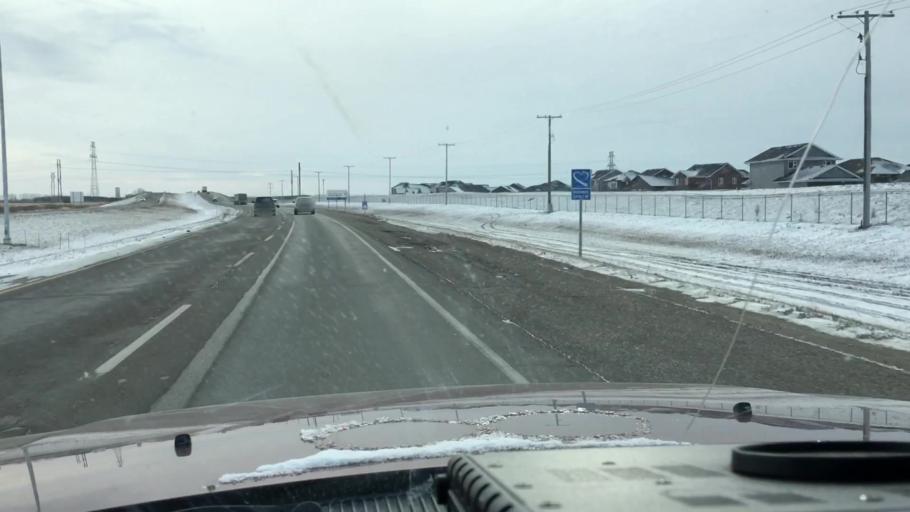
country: CA
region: Saskatchewan
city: Saskatoon
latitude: 52.0765
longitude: -106.6049
